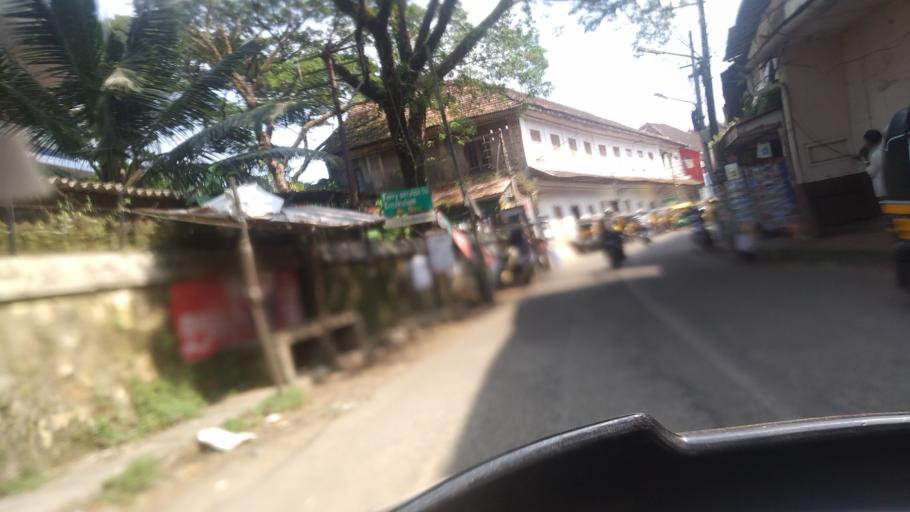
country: IN
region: Kerala
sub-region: Ernakulam
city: Cochin
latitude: 9.9688
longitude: 76.2512
